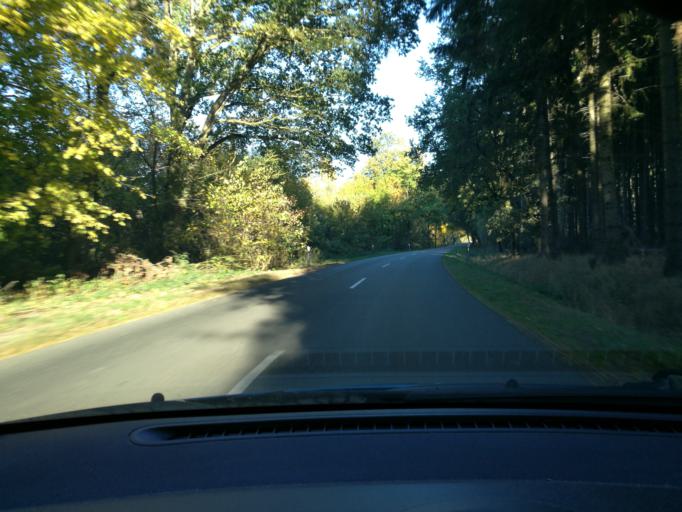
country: DE
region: Lower Saxony
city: Ludersburg
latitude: 53.3285
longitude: 10.5865
